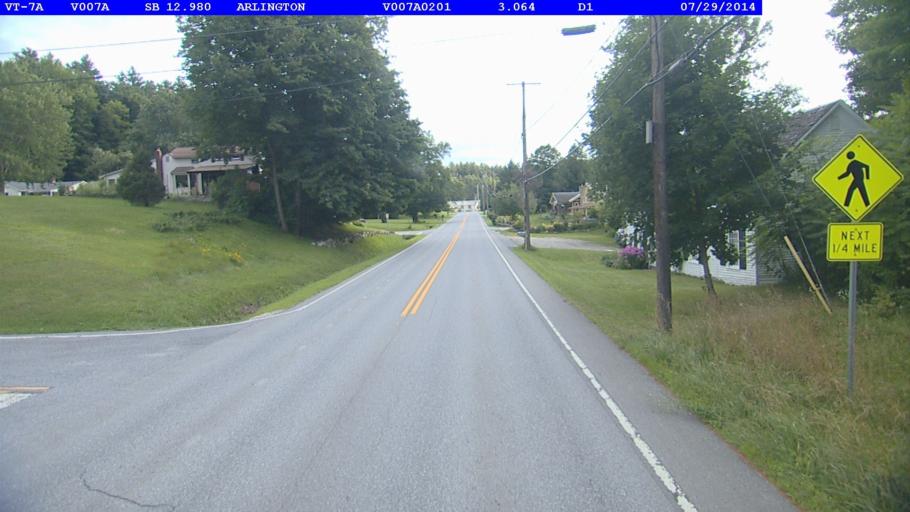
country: US
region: Vermont
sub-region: Bennington County
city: Arlington
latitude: 43.0632
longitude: -73.1579
